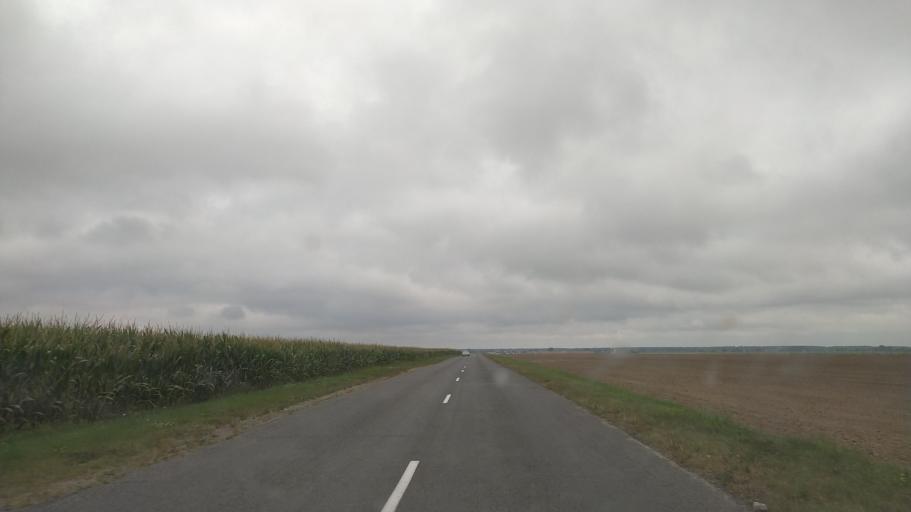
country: BY
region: Brest
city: Byaroza
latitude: 52.5662
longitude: 24.8994
